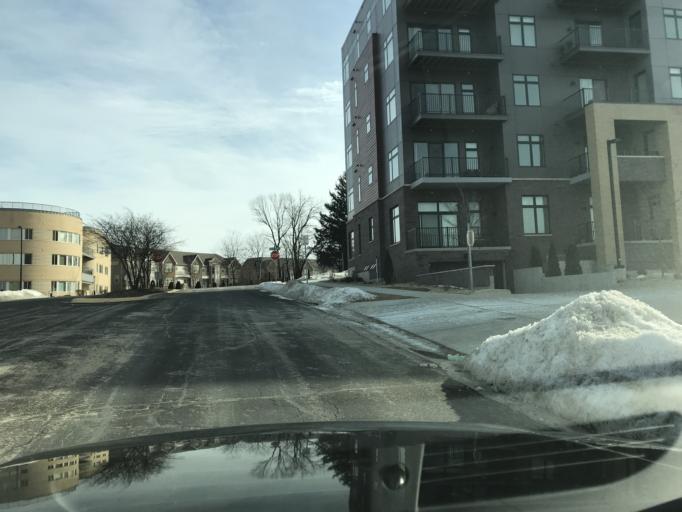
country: US
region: Wisconsin
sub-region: Dane County
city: Monona
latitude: 43.0866
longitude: -89.2804
